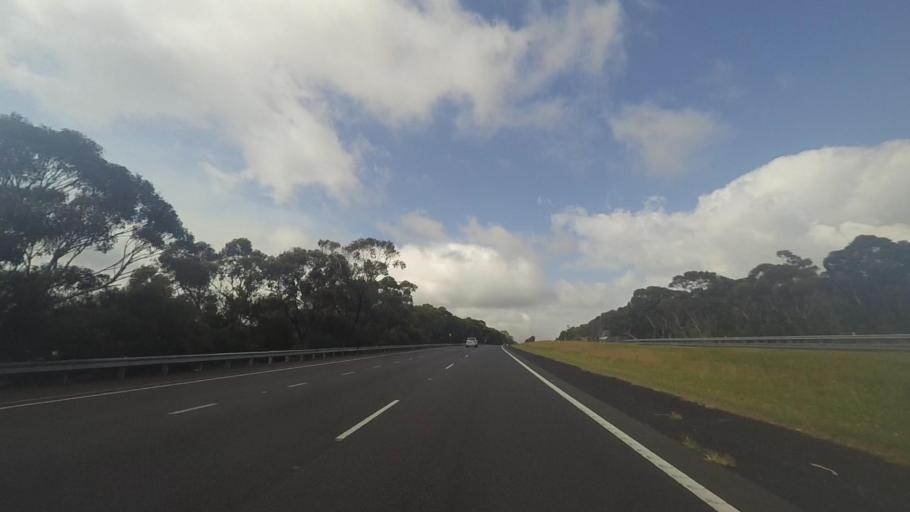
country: AU
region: New South Wales
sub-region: Wollongong
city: Helensburgh
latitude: -34.2072
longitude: 150.9633
